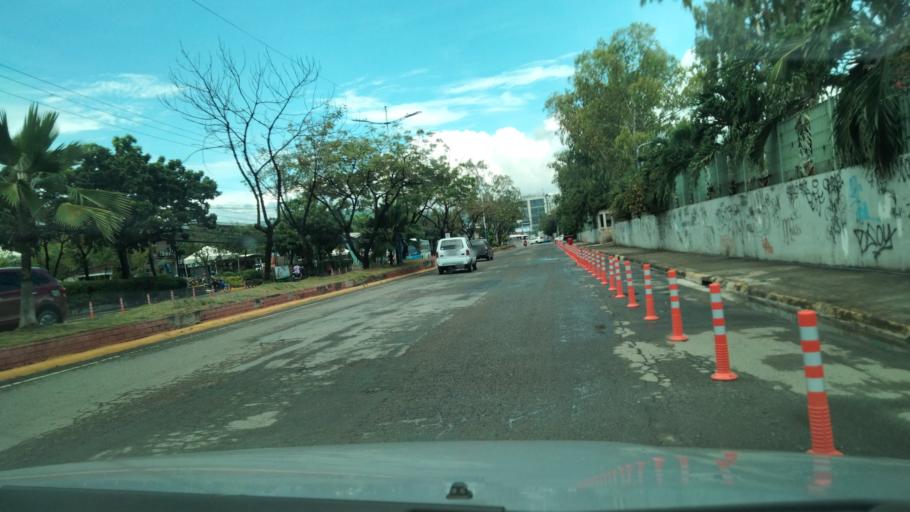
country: PH
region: Central Visayas
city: Mandaue City
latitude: 10.3256
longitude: 123.9356
